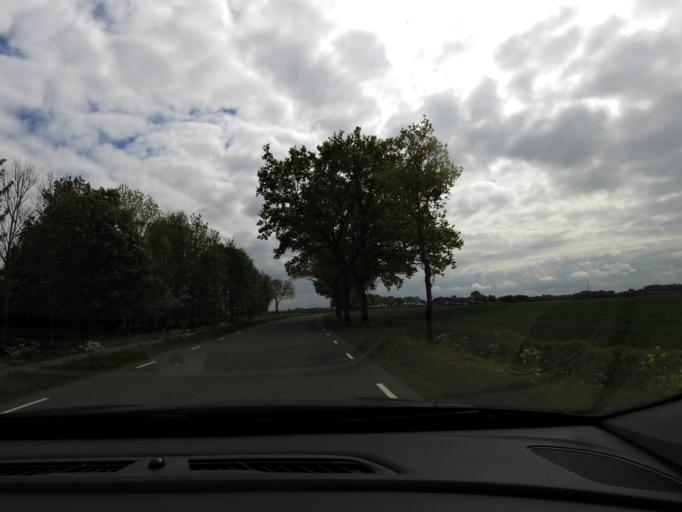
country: NL
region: Gelderland
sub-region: Gemeente Tiel
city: Tiel
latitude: 51.9330
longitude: 5.4509
